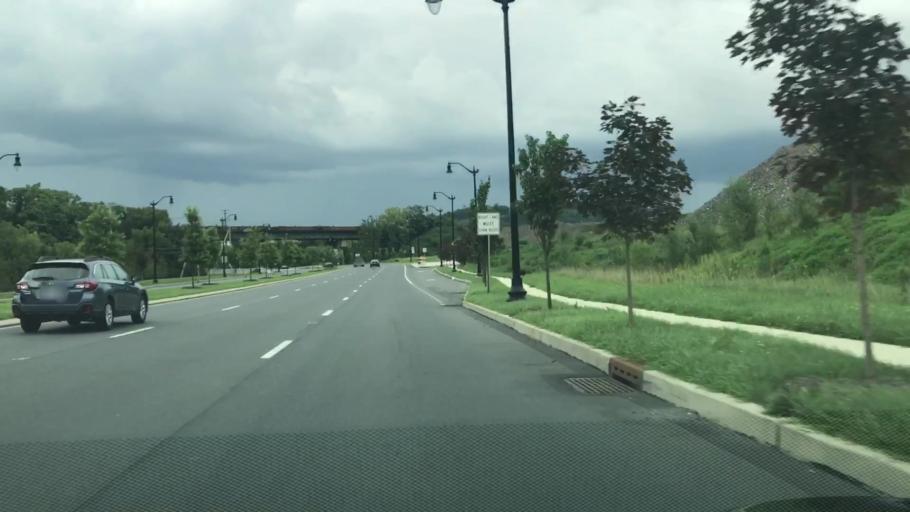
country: US
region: Pennsylvania
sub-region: Northampton County
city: Freemansburg
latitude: 40.6057
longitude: -75.3403
